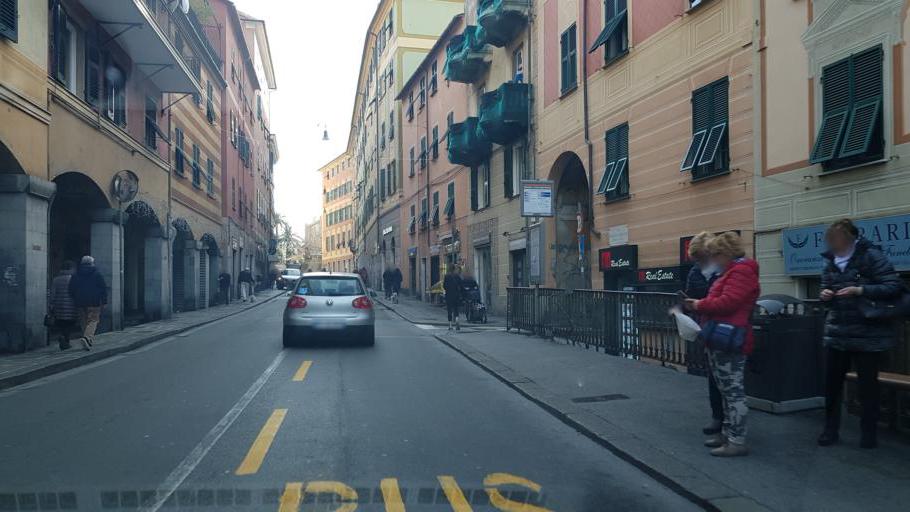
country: IT
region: Liguria
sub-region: Provincia di Genova
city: Bogliasco
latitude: 44.3844
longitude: 9.0357
